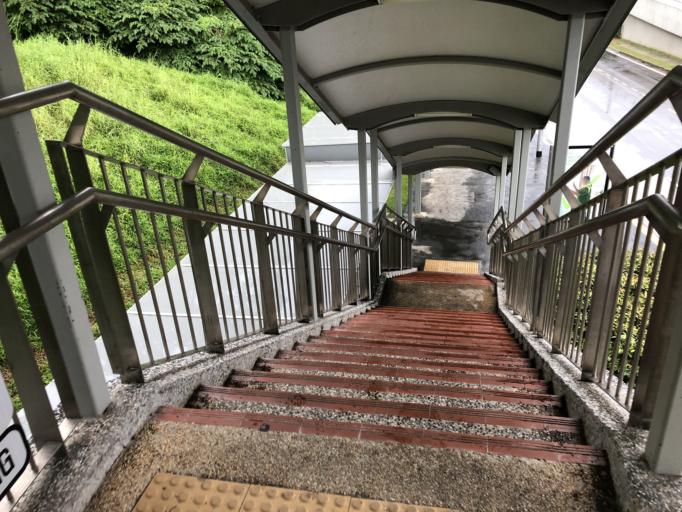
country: MY
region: Johor
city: Johor Bahru
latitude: 1.3600
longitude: 103.7669
